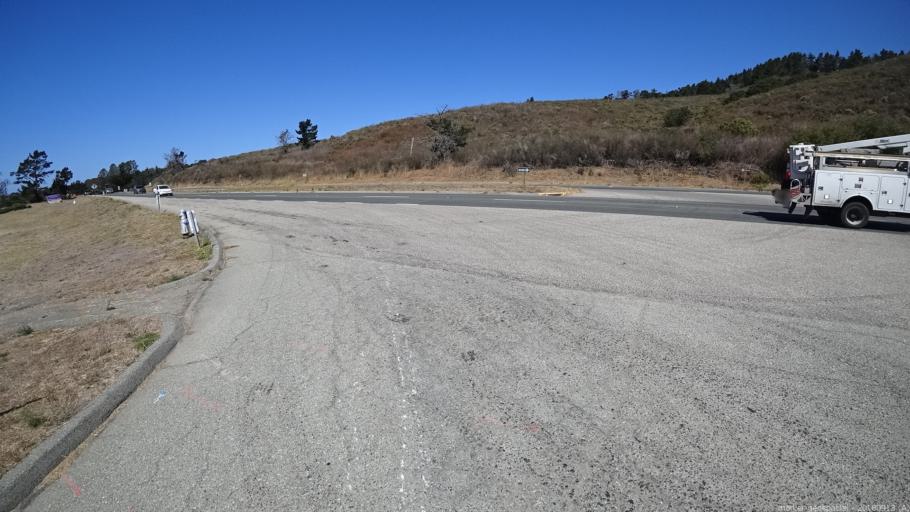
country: US
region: California
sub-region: Monterey County
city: Carmel-by-the-Sea
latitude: 36.5427
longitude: -121.8921
